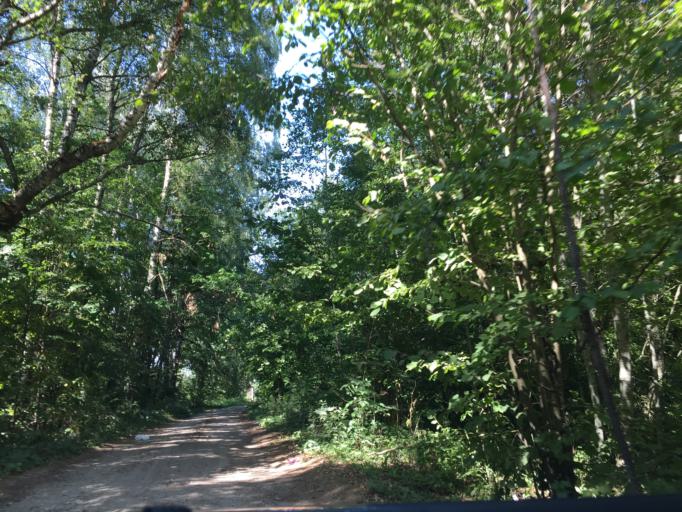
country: LT
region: Siauliu apskritis
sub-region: Joniskis
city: Joniskis
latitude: 56.3347
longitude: 23.5598
